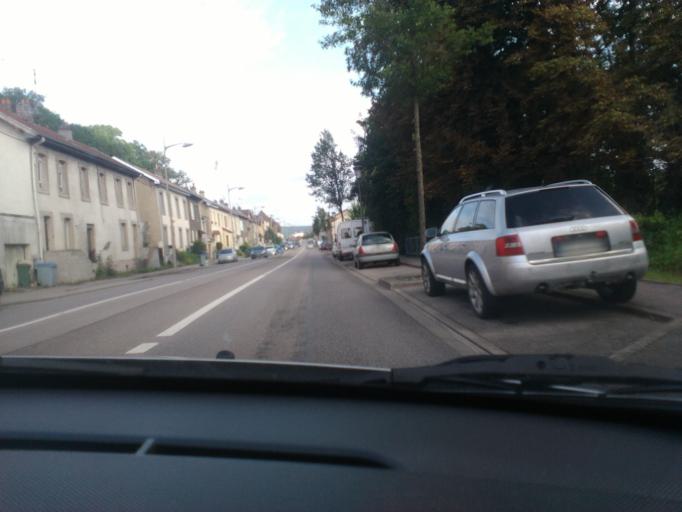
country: FR
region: Lorraine
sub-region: Departement de Meurthe-et-Moselle
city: Frouard
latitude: 48.7502
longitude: 6.1468
